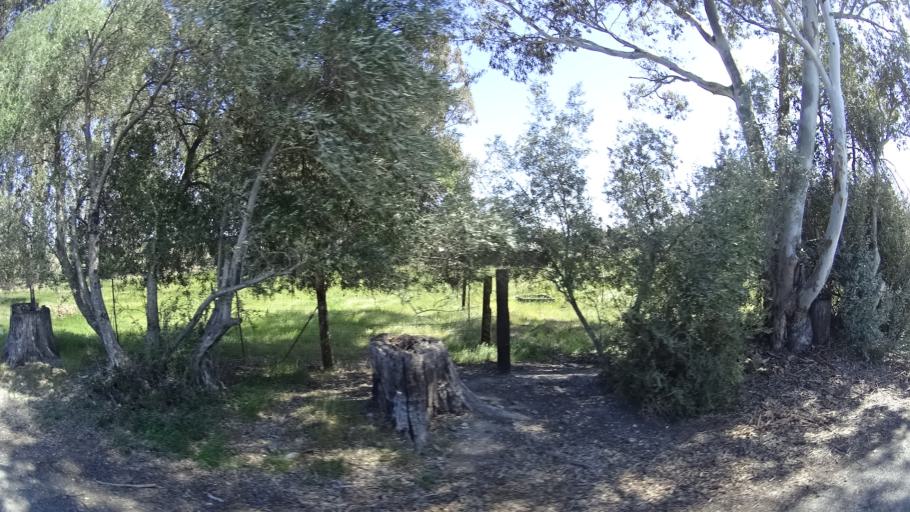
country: US
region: California
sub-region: Glenn County
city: Orland
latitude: 39.7711
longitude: -122.2296
